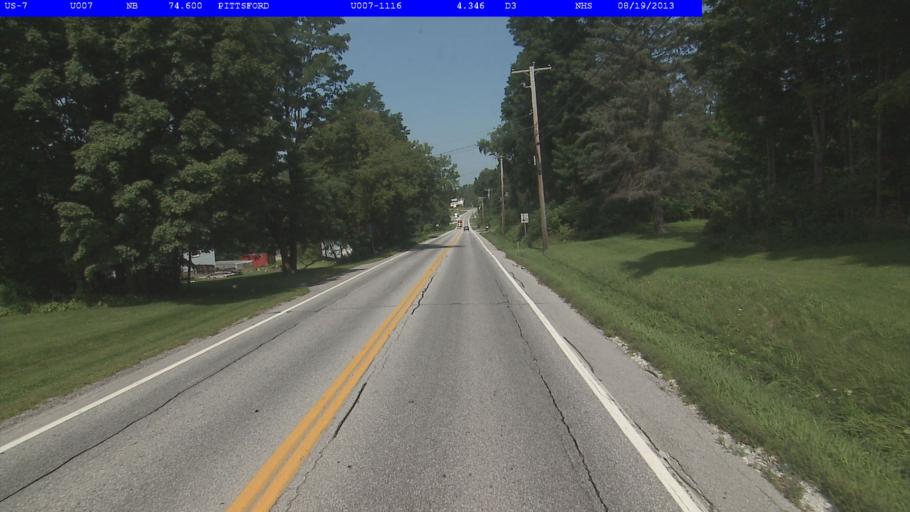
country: US
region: Vermont
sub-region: Rutland County
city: Brandon
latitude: 43.7107
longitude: -73.0329
